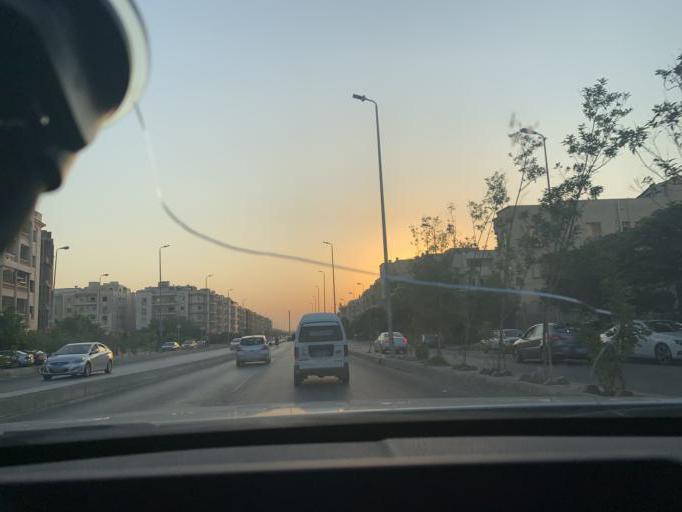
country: EG
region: Muhafazat al Qahirah
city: Cairo
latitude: 30.0060
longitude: 31.4539
